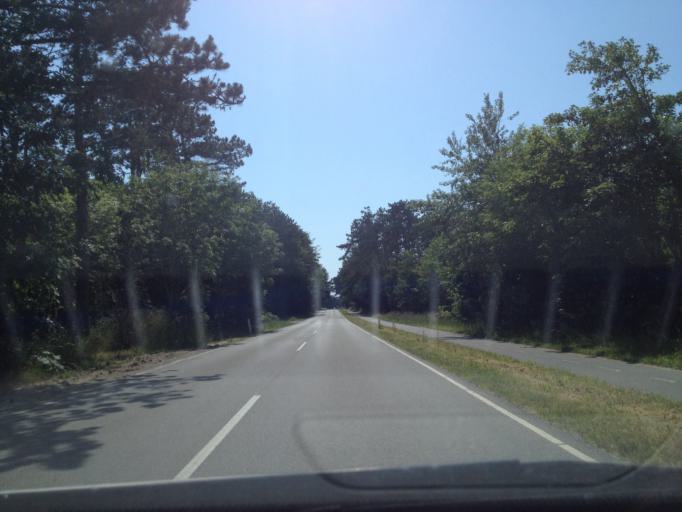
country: DK
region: Central Jutland
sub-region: Samso Kommune
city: Tranebjerg
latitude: 55.8665
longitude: 10.5823
